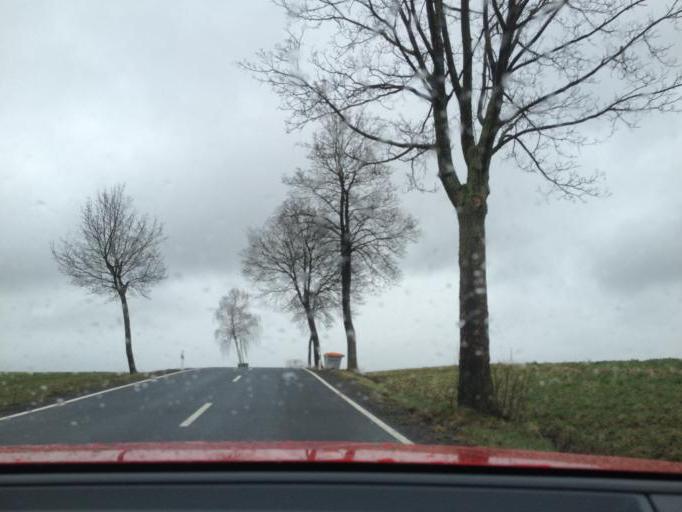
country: DE
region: Bavaria
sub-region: Upper Franconia
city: Thiersheim
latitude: 50.0801
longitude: 12.1601
